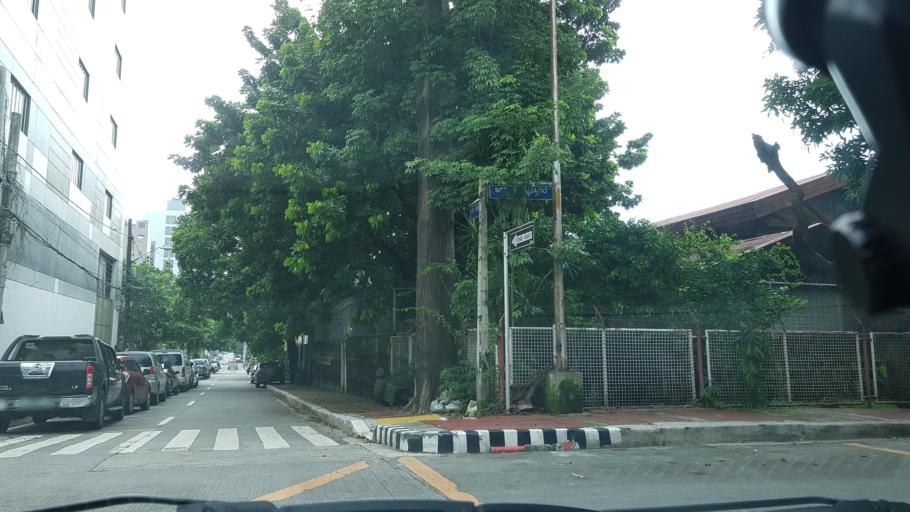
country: PH
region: Calabarzon
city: Del Monte
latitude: 14.6305
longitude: 121.0278
